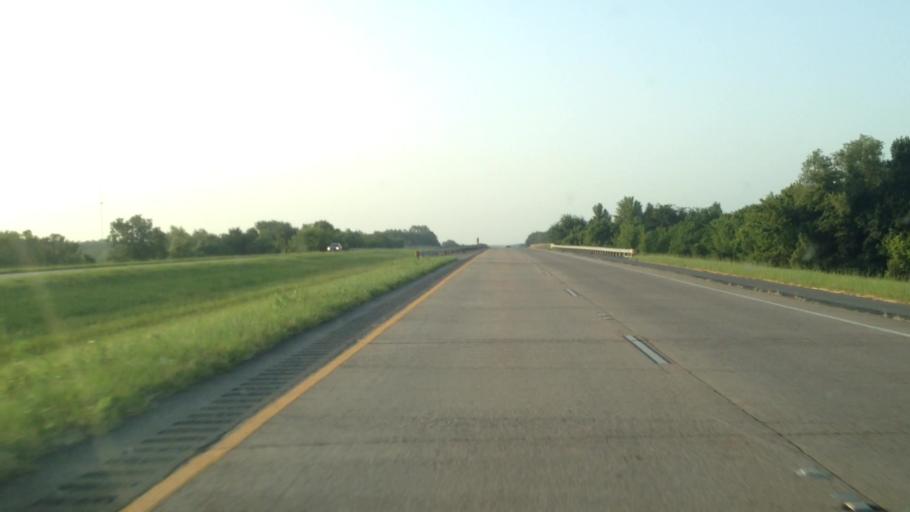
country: US
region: Louisiana
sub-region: Natchitoches Parish
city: Vienna Bend
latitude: 31.6259
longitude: -93.0655
